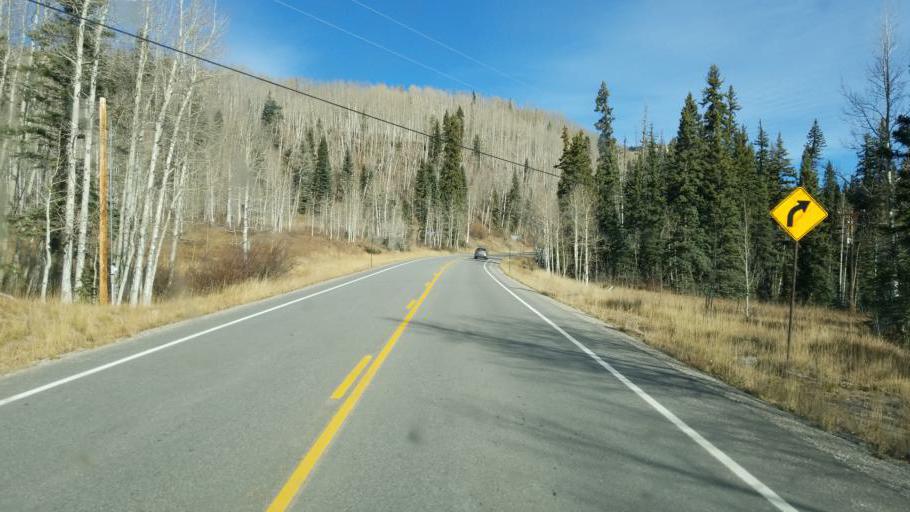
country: US
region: Colorado
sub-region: San Juan County
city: Silverton
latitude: 37.6632
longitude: -107.7980
